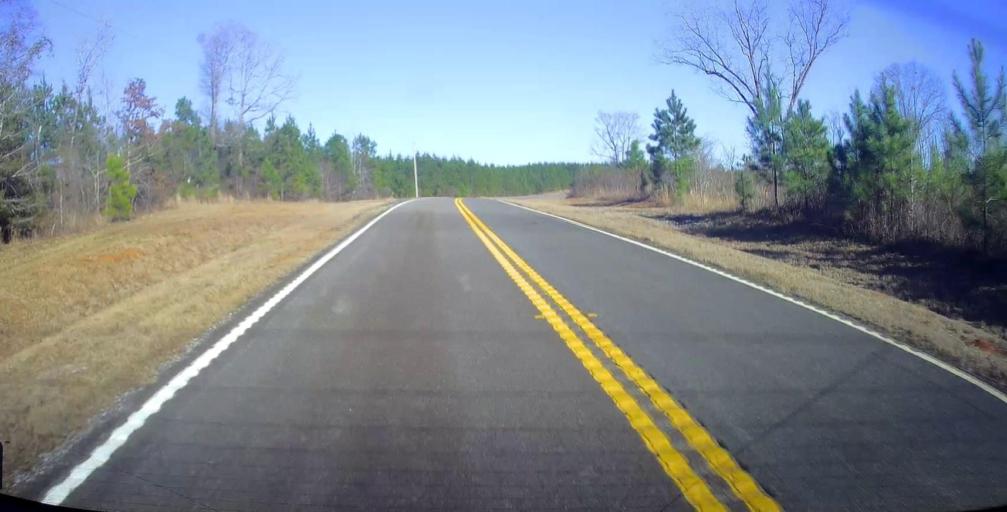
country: US
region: Georgia
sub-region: Talbot County
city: Talbotton
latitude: 32.6502
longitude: -84.3931
